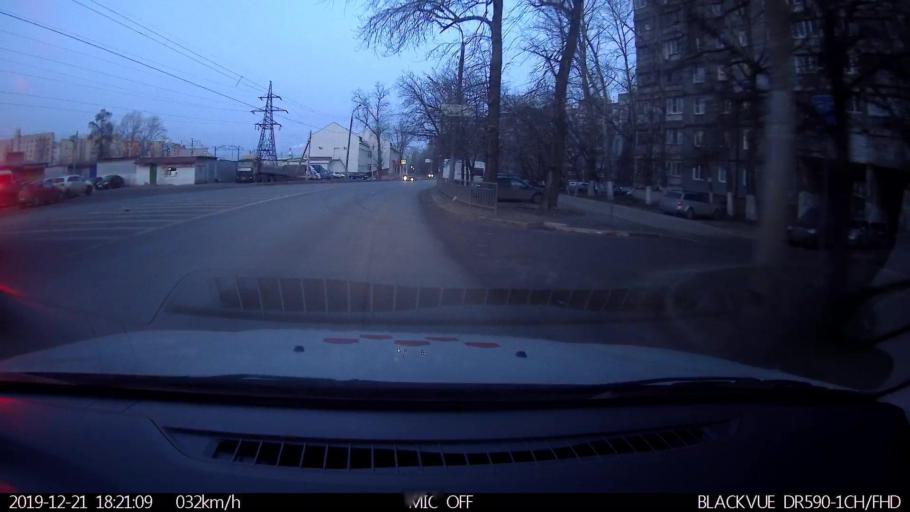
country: RU
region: Nizjnij Novgorod
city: Nizhniy Novgorod
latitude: 56.3343
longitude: 43.9304
